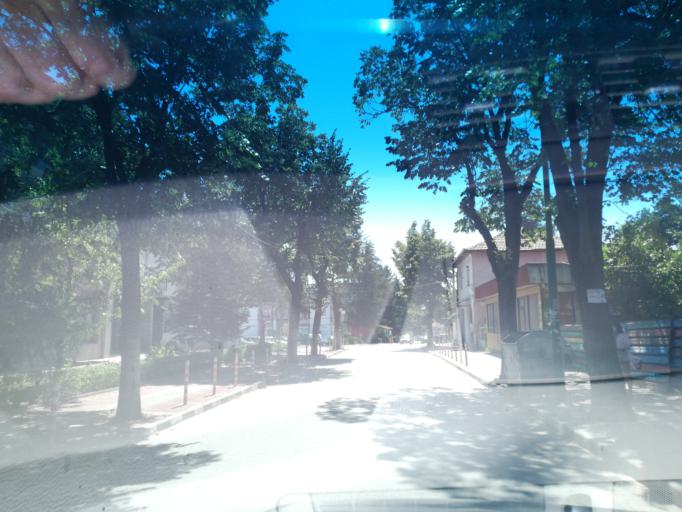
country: BG
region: Pazardzhik
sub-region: Obshtina Strelcha
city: Strelcha
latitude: 42.5068
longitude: 24.3208
